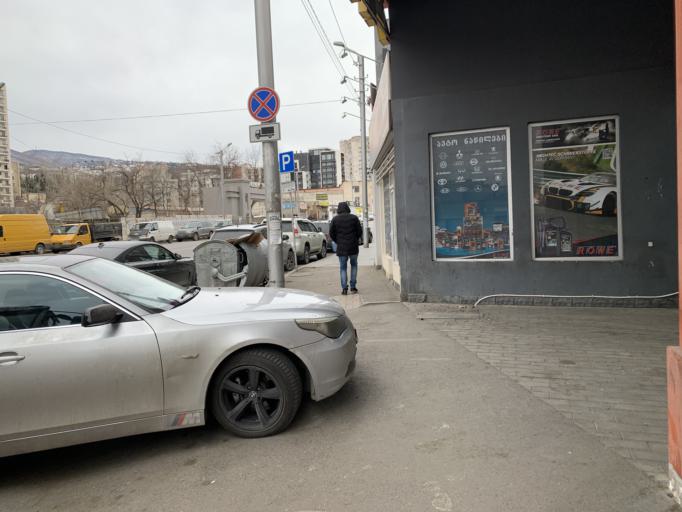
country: GE
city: Tsqnet'i
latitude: 41.7219
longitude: 44.7372
